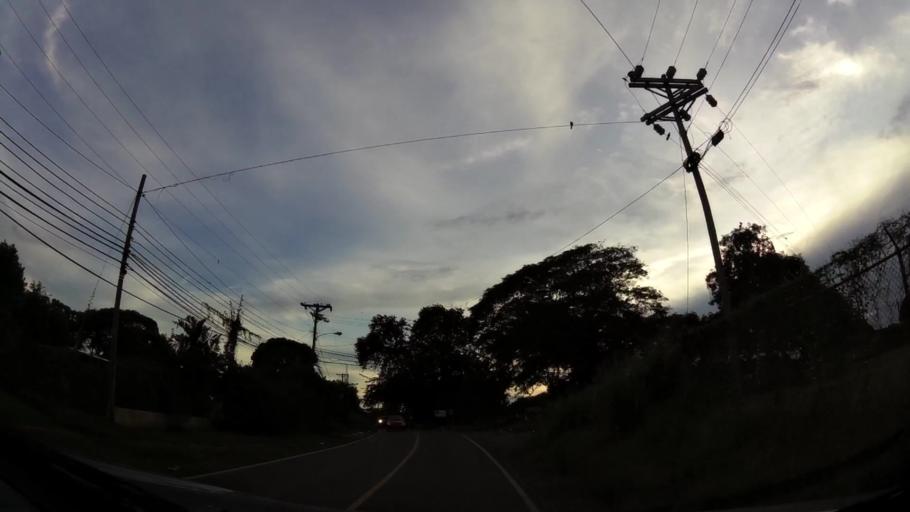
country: PA
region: Panama
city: La Chorrera
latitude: 8.8648
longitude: -79.7656
